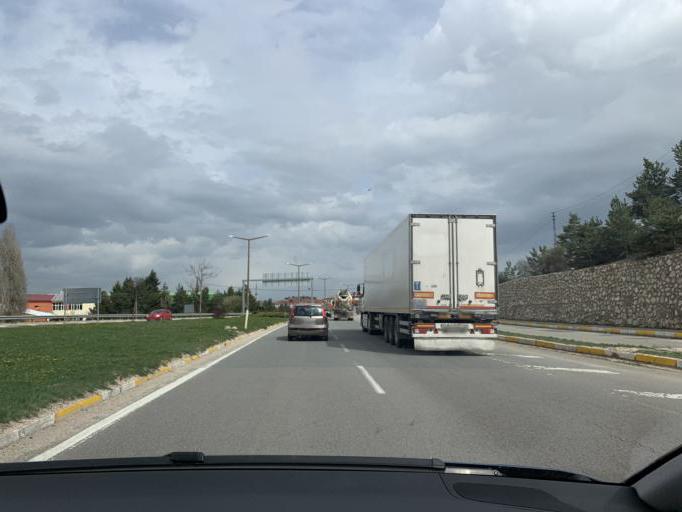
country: TR
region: Bolu
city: Gerede
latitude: 40.7988
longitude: 32.1858
